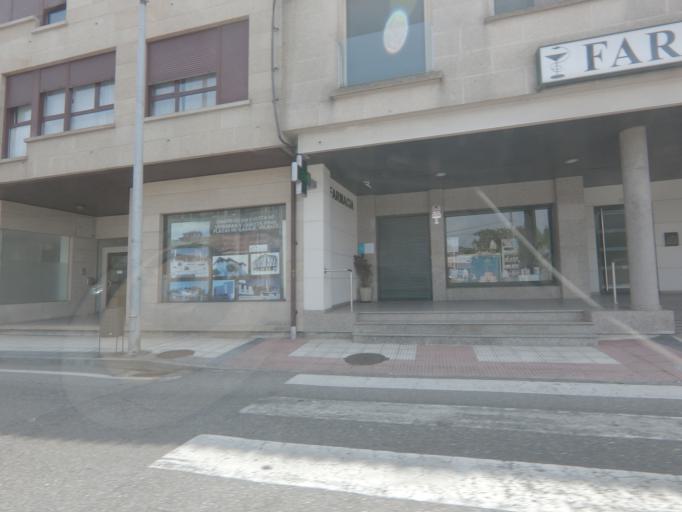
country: ES
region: Galicia
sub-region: Provincia de Pontevedra
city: A Guarda
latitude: 41.9060
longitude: -8.8629
